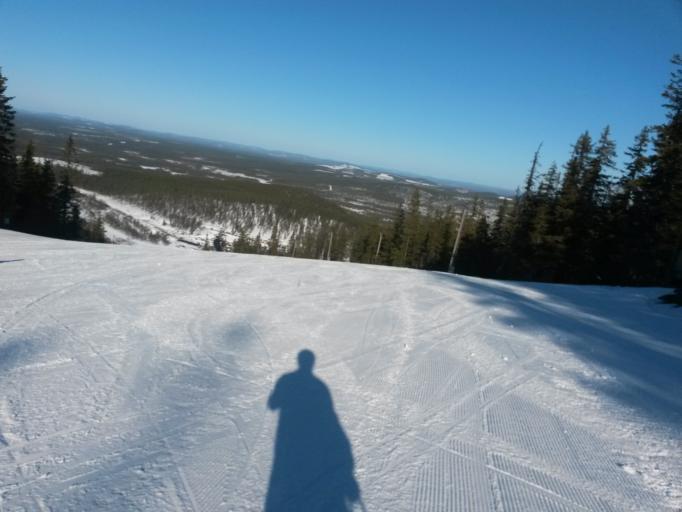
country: SE
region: Vaesterbotten
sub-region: Skelleftea Kommun
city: Langsele
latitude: 65.1554
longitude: 20.1371
